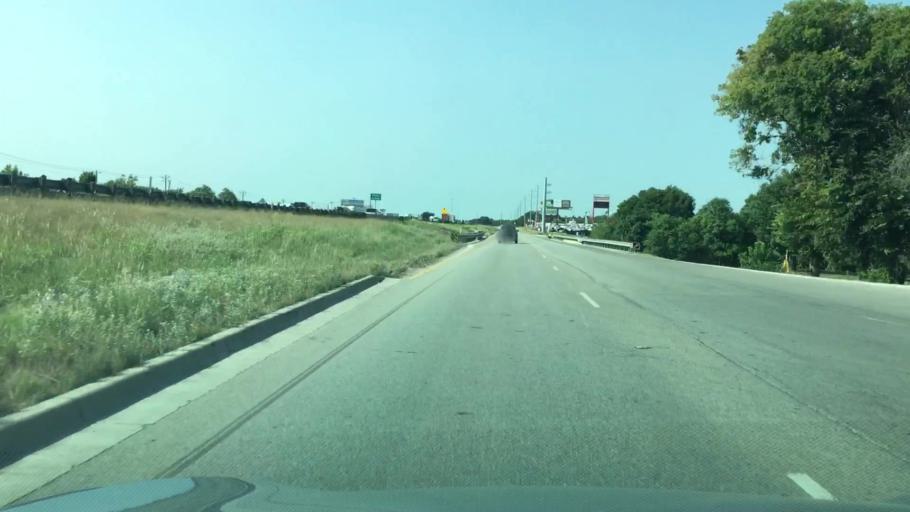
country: US
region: Texas
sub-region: Hays County
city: Kyle
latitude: 30.0042
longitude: -97.8662
